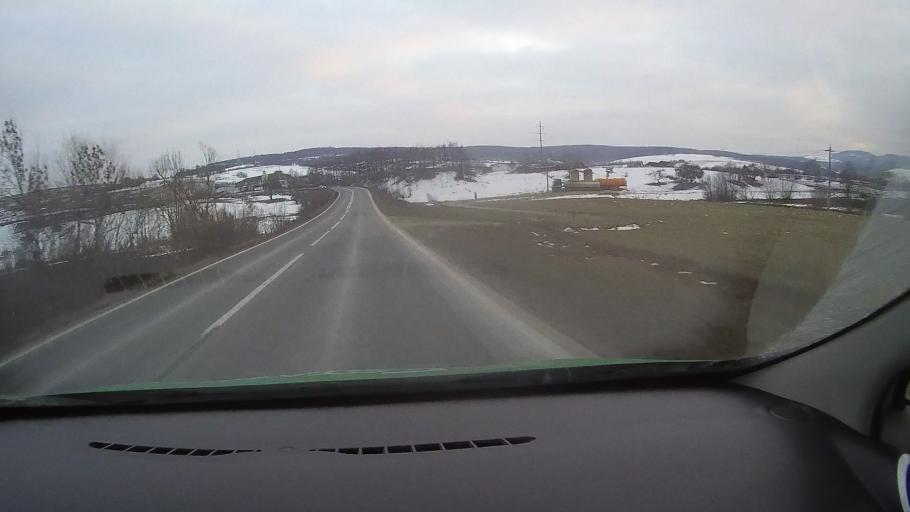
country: RO
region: Harghita
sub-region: Comuna Lupeni
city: Lupeni
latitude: 46.3575
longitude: 25.2389
